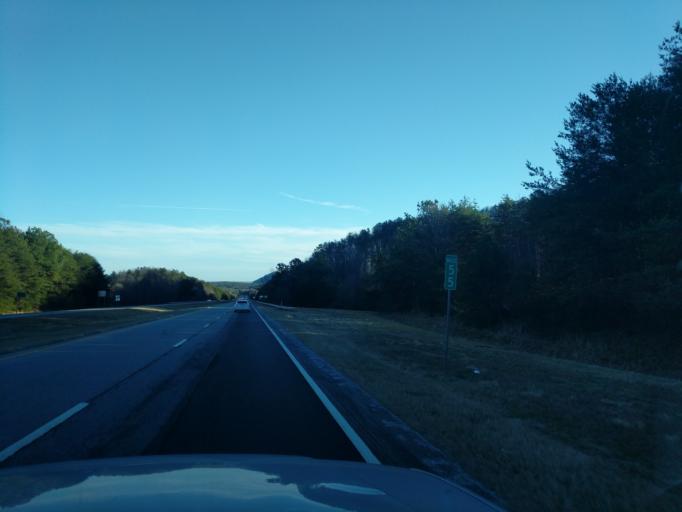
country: US
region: Georgia
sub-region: Stephens County
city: Toccoa
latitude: 34.5842
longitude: -83.4115
